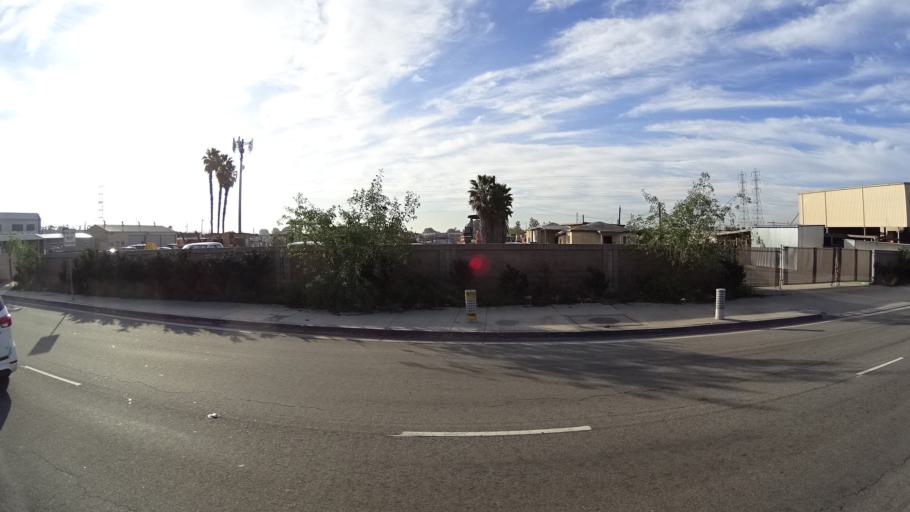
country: US
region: California
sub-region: Orange County
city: Stanton
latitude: 33.8029
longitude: -117.9909
